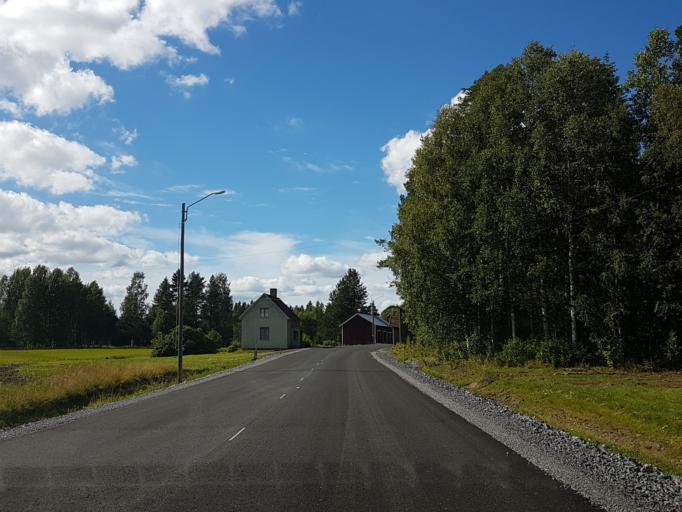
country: SE
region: Vaesterbotten
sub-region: Robertsfors Kommun
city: Robertsfors
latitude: 64.1383
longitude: 20.6226
